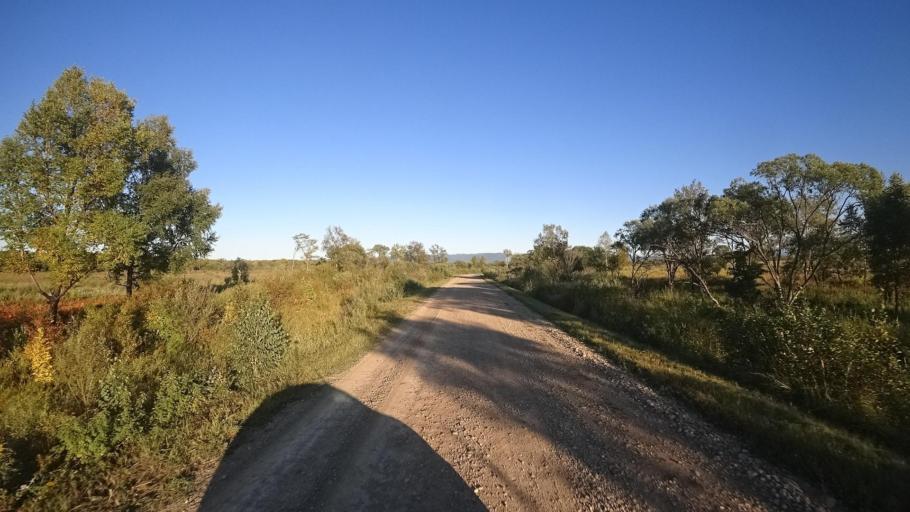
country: RU
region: Primorskiy
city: Kirovskiy
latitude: 44.8149
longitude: 133.6130
